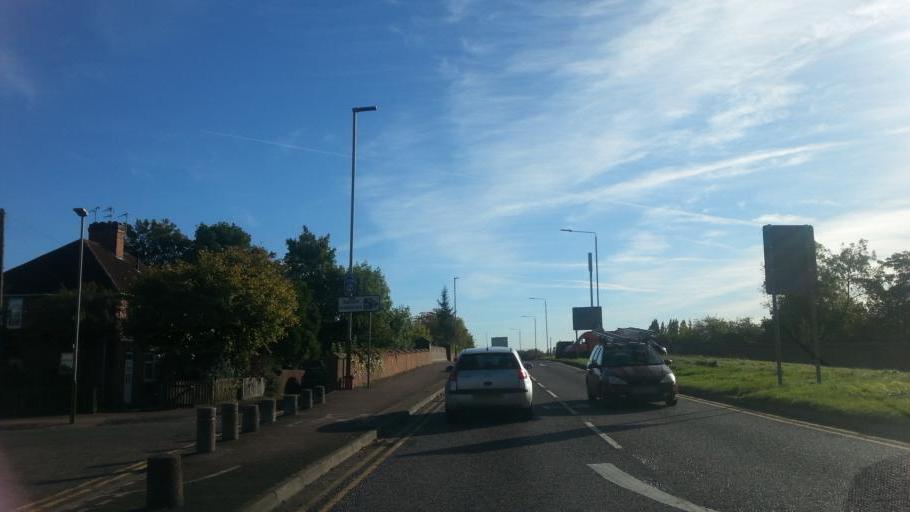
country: GB
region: England
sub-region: Leicestershire
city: Wigston Magna
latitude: 52.5971
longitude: -1.1280
